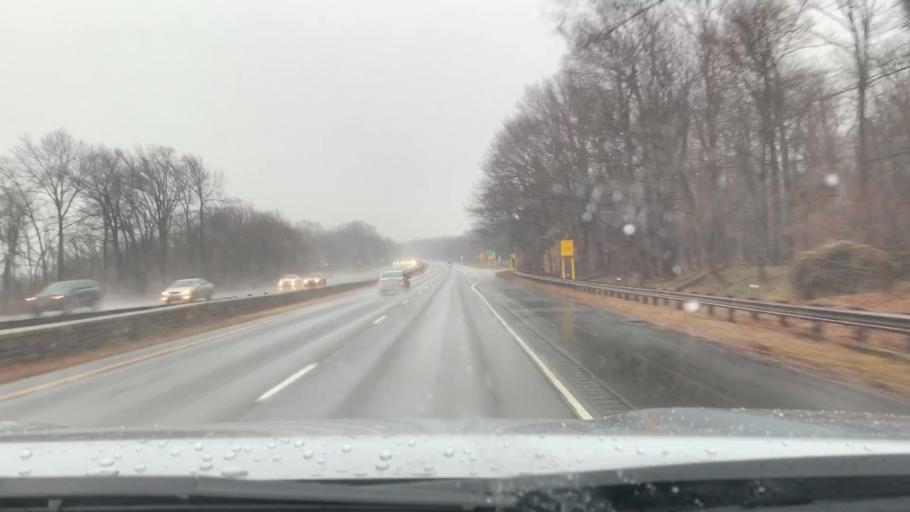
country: US
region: New Jersey
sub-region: Bergen County
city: Englewood Cliffs
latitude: 40.8832
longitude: -73.9468
